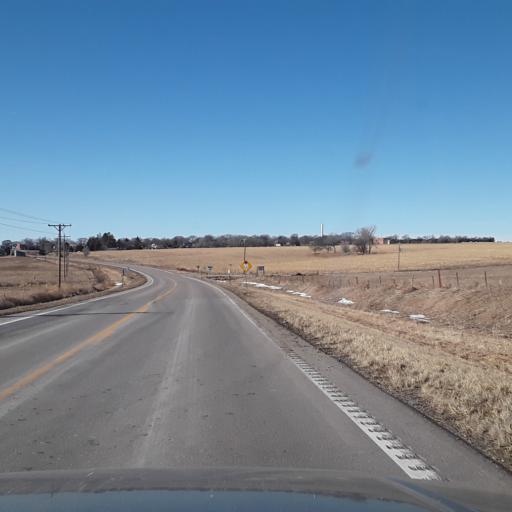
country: US
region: Nebraska
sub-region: Dawson County
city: Gothenburg
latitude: 40.7050
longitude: -100.2024
